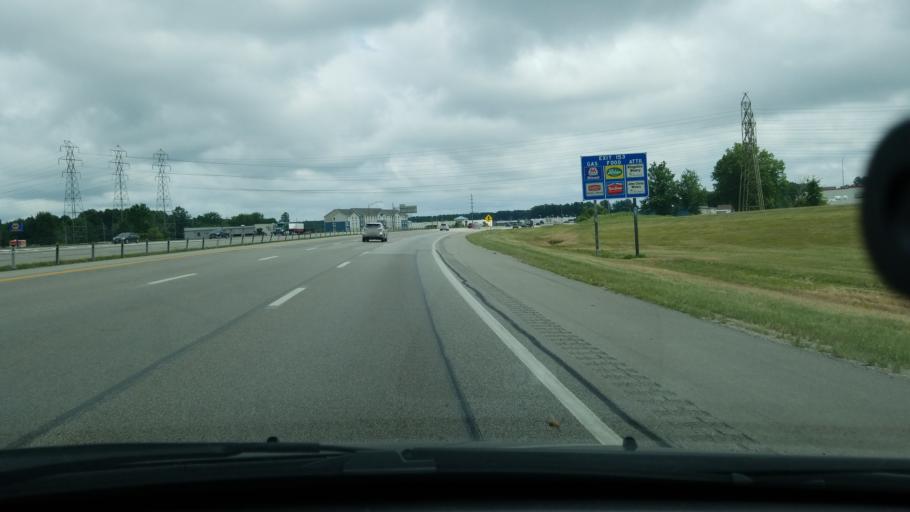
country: US
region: Ohio
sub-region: Lorain County
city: Avon
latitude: 41.4640
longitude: -82.0528
